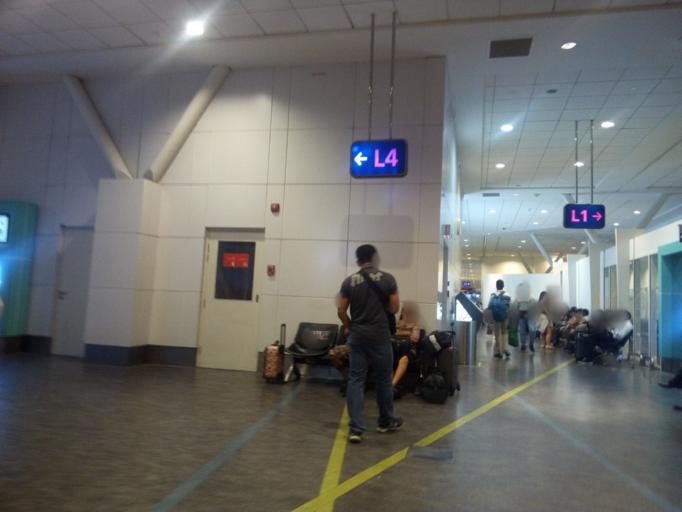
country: MY
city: Sungai Pelek New Village
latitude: 2.7413
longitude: 101.6872
